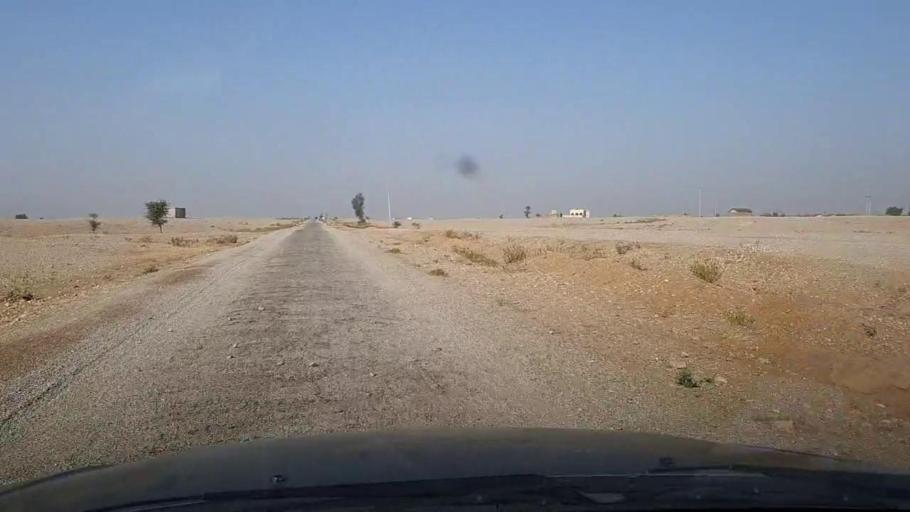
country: PK
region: Sindh
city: Sann
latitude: 26.0092
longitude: 68.0887
